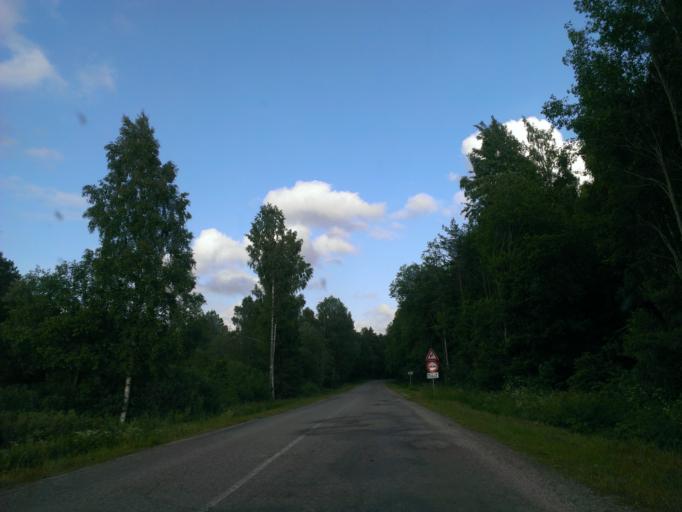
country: LV
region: Skrunda
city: Skrunda
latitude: 56.6896
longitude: 21.8773
